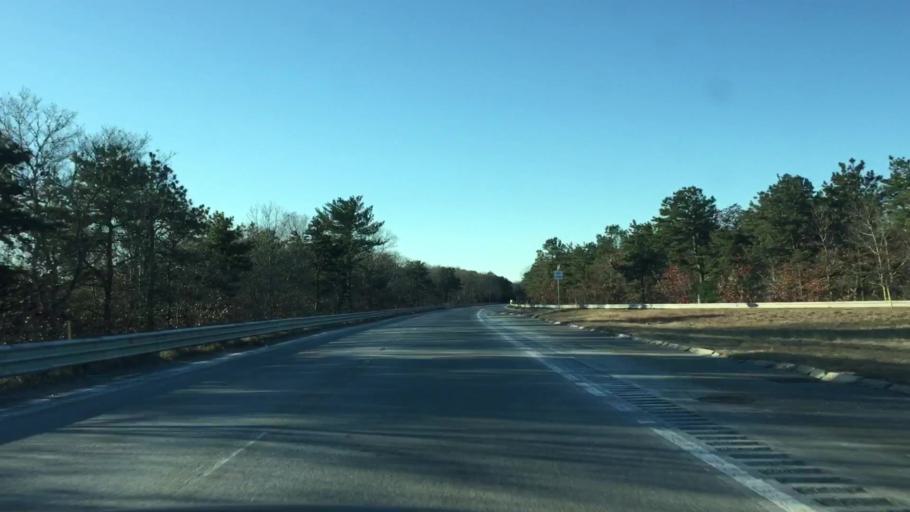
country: US
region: Massachusetts
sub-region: Barnstable County
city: North Falmouth
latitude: 41.6429
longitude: -70.6056
